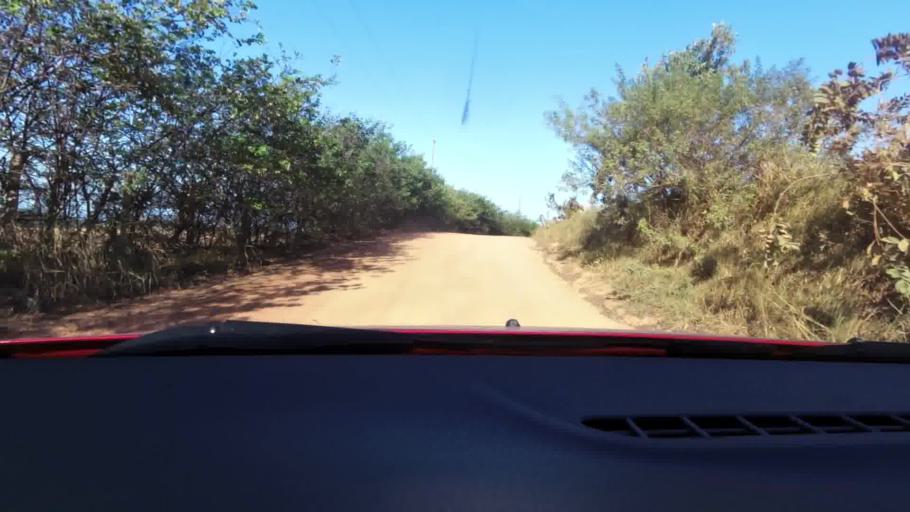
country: BR
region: Espirito Santo
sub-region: Guarapari
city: Guarapari
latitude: -20.5391
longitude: -40.4330
